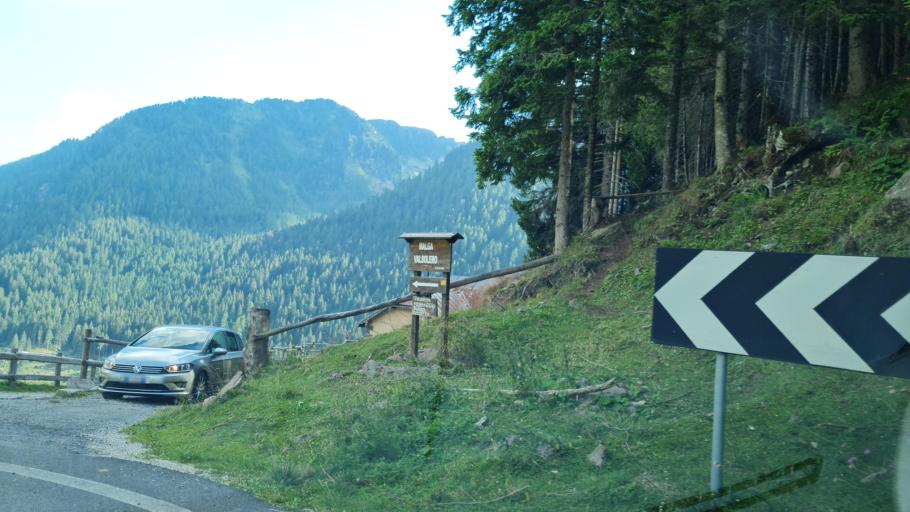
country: IT
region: Trentino-Alto Adige
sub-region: Provincia di Trento
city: Torcegno
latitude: 46.1585
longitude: 11.4338
